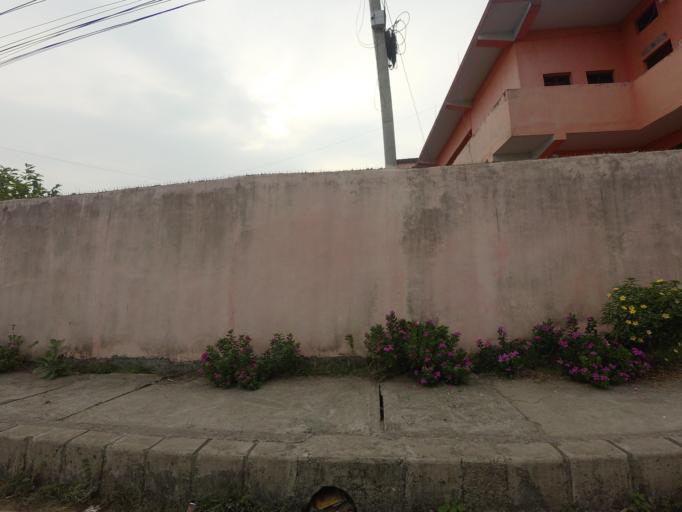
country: NP
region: Western Region
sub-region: Lumbini Zone
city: Bhairahawa
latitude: 27.4967
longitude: 83.4524
